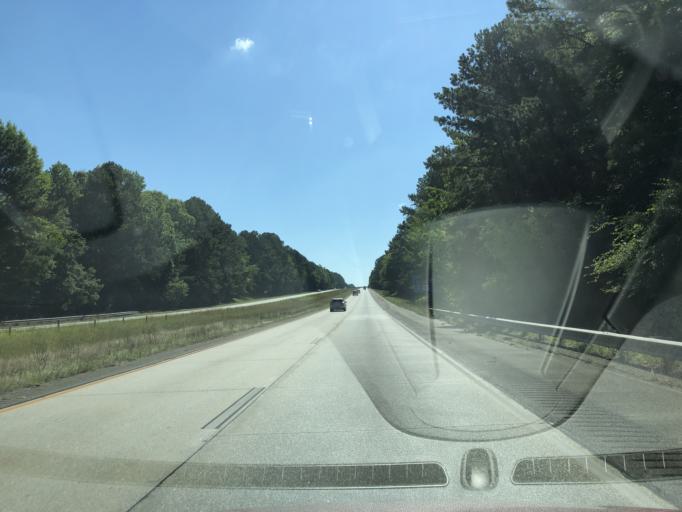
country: US
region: Georgia
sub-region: McDuffie County
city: Thomson
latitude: 33.5075
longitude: -82.5349
